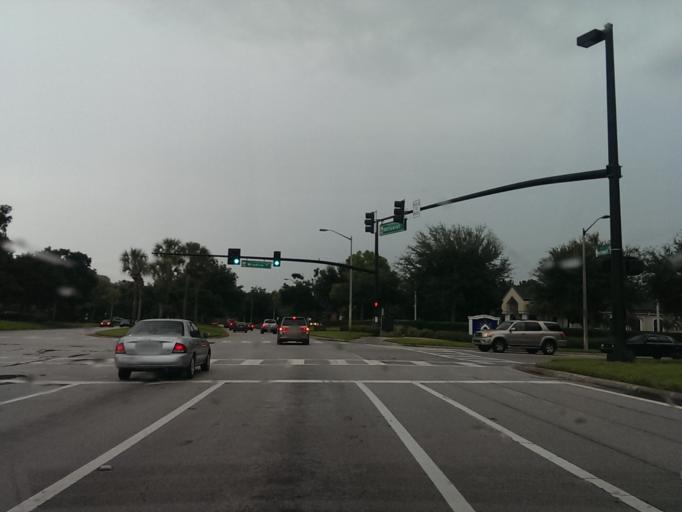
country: US
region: Florida
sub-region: Orange County
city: Orlovista
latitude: 28.5138
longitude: -81.4640
